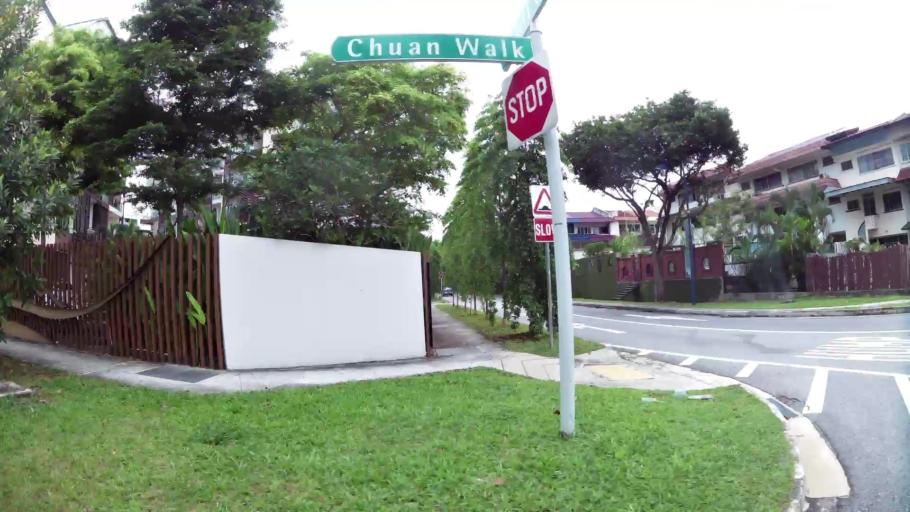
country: SG
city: Singapore
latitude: 1.3556
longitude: 103.8660
